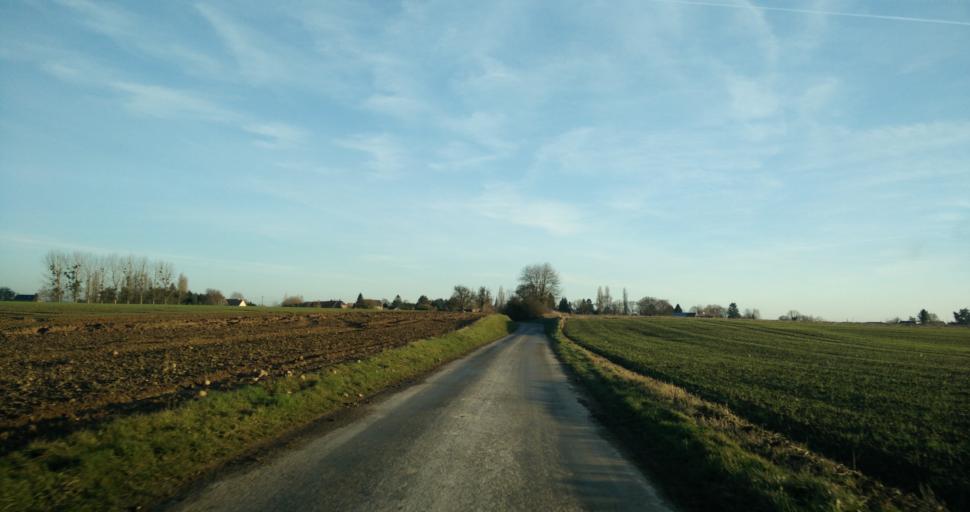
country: FR
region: Haute-Normandie
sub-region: Departement de l'Eure
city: Saint-Pierre-des-Fleurs
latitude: 49.1724
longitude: 1.0009
